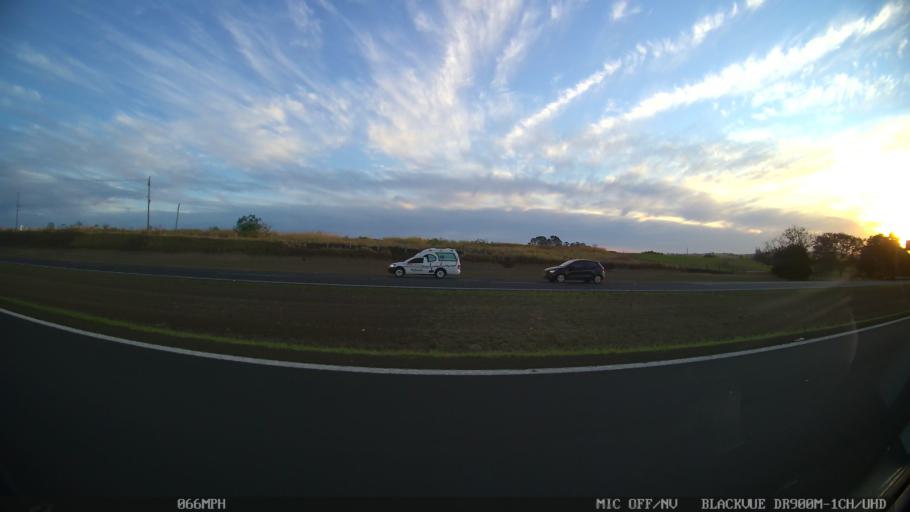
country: BR
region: Sao Paulo
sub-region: Pindorama
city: Pindorama
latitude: -21.2054
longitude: -48.9351
